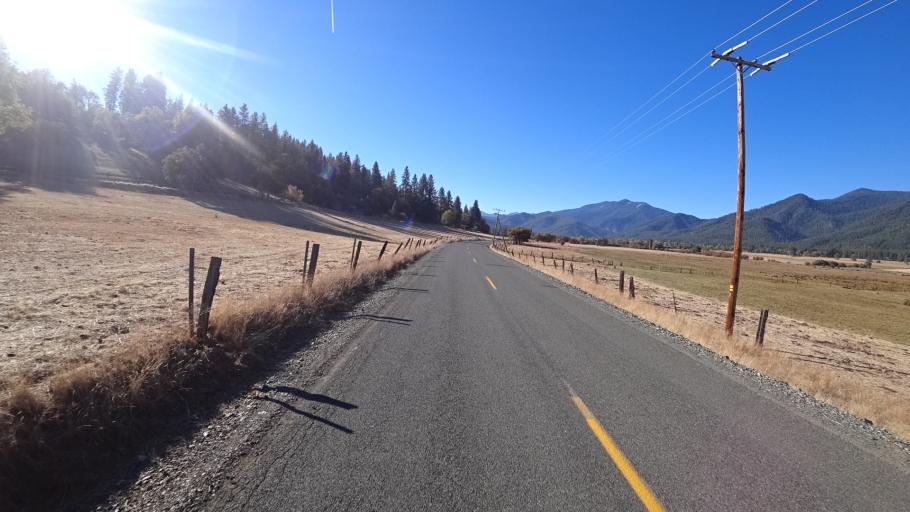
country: US
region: California
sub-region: Siskiyou County
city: Yreka
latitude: 41.4754
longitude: -122.8787
